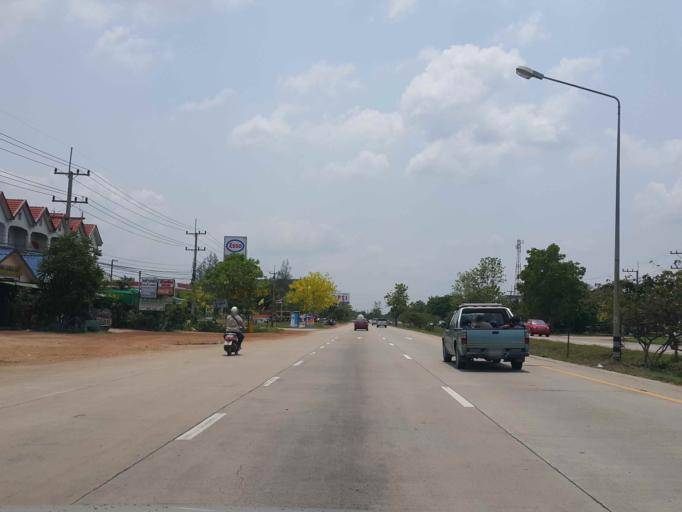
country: TH
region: Lampang
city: Ko Kha
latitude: 18.2195
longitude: 99.4247
